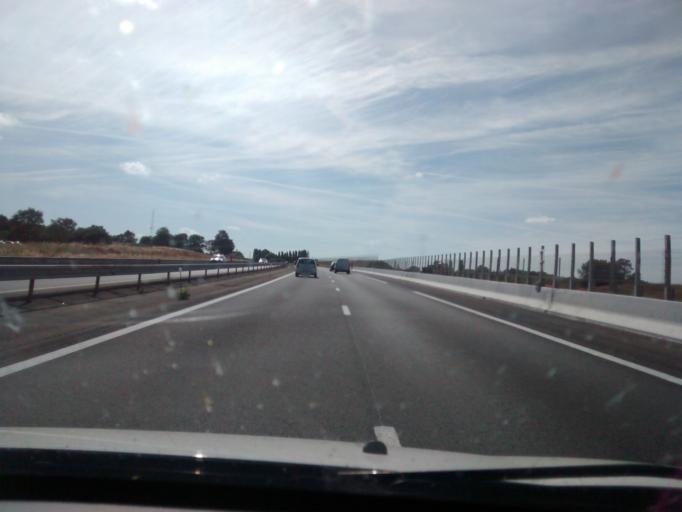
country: FR
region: Pays de la Loire
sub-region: Departement de la Mayenne
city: Change
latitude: 48.1160
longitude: -0.7826
